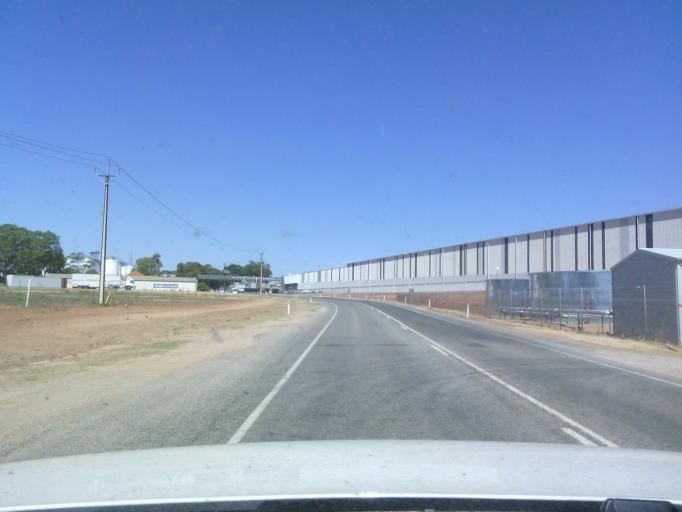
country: AU
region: South Australia
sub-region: Berri and Barmera
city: Monash
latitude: -34.2781
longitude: 140.5386
